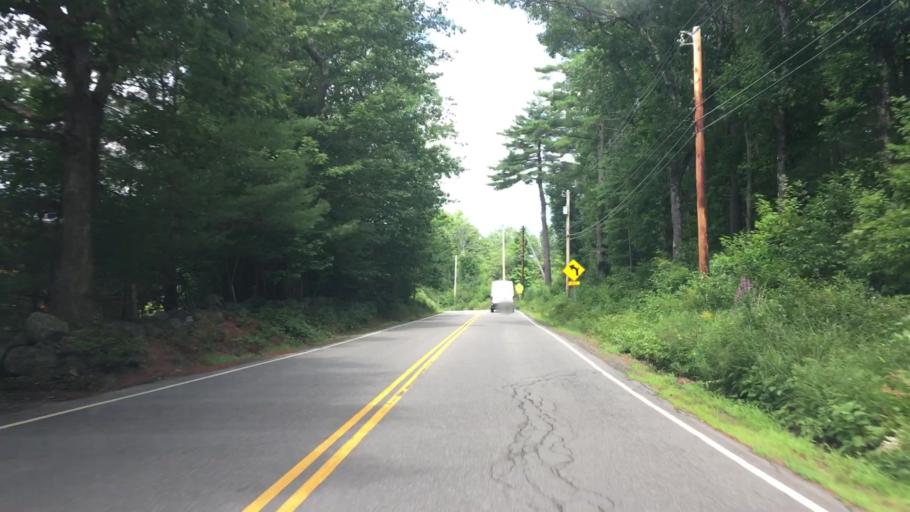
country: US
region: New Hampshire
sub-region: Belknap County
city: Meredith
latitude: 43.6201
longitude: -71.5425
